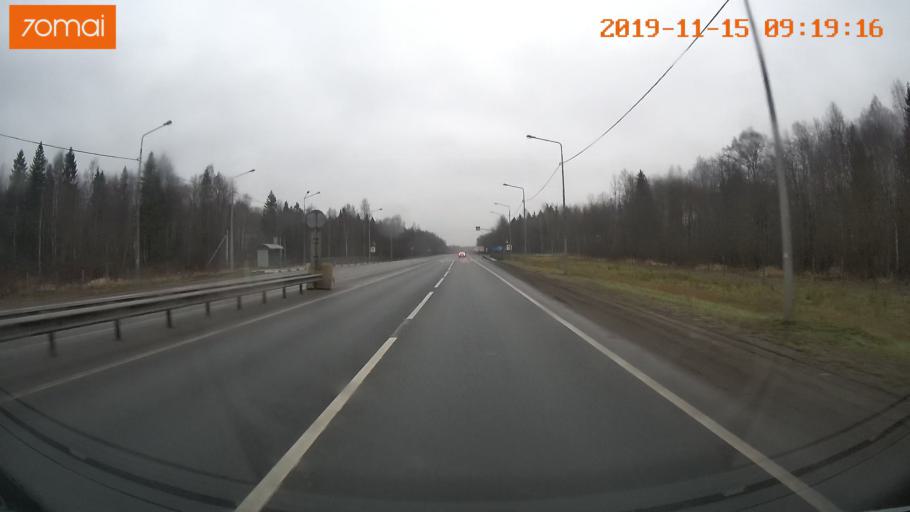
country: RU
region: Vologda
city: Tonshalovo
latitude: 59.2824
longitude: 38.0129
